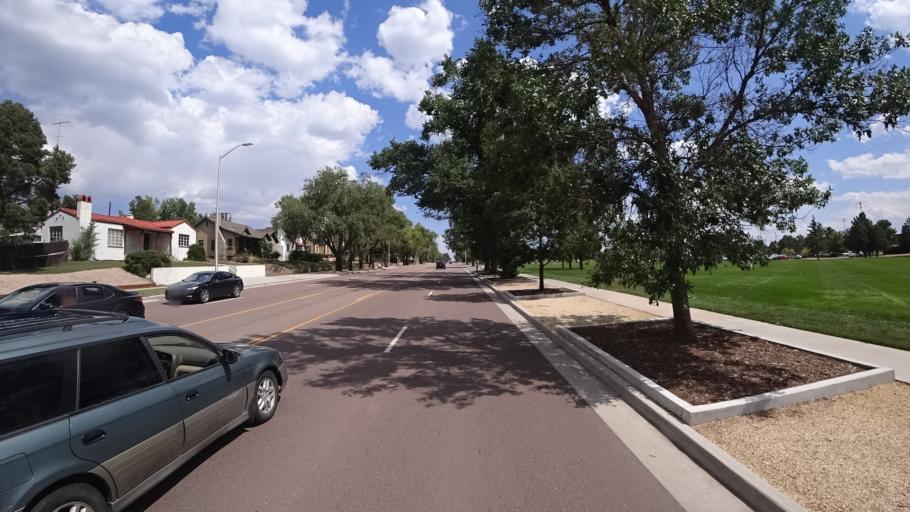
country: US
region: Colorado
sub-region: El Paso County
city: Colorado Springs
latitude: 38.8332
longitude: -104.8020
